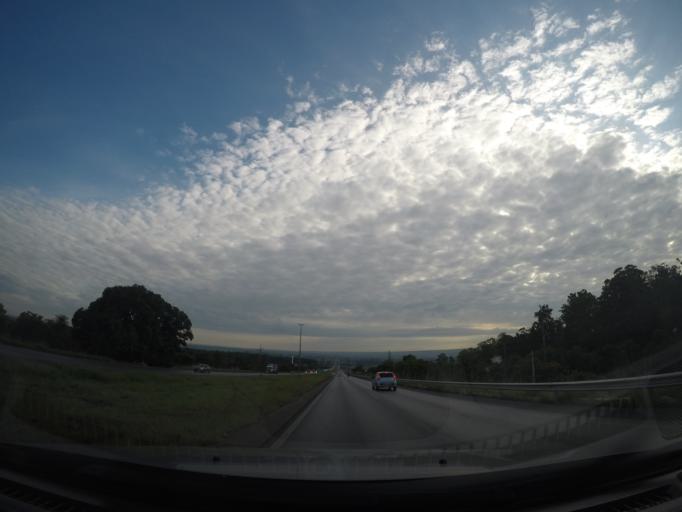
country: BR
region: Goias
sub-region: Planaltina
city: Planaltina
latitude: -15.6176
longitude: -47.7103
